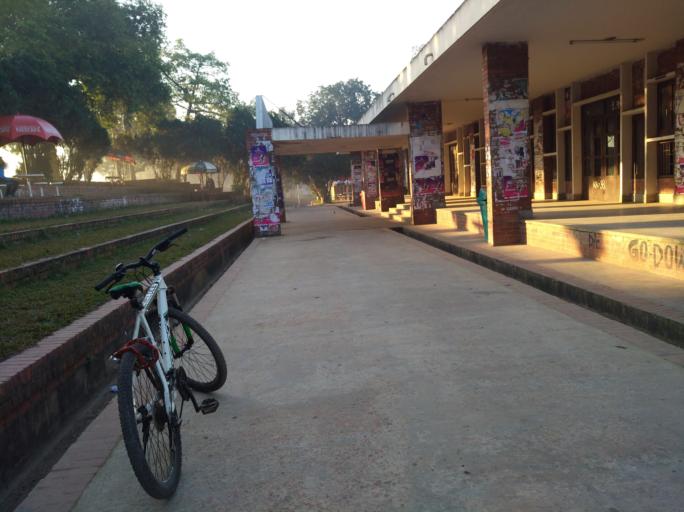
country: BD
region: Dhaka
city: Tungi
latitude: 23.8795
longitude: 90.2709
